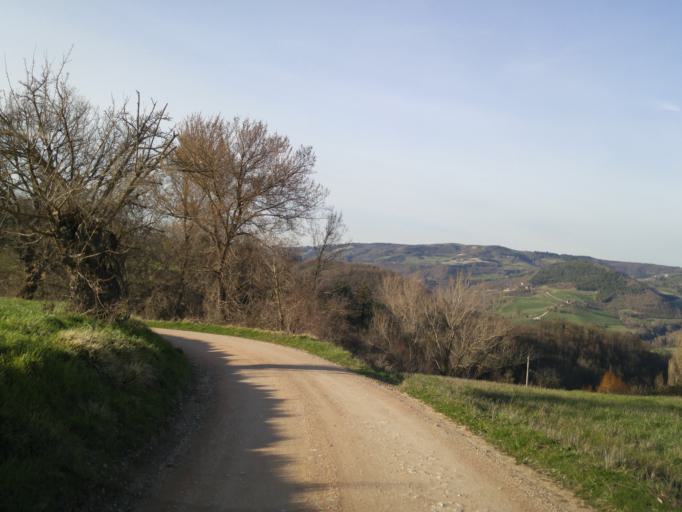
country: IT
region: The Marches
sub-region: Provincia di Pesaro e Urbino
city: Canavaccio
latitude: 43.6855
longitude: 12.6874
